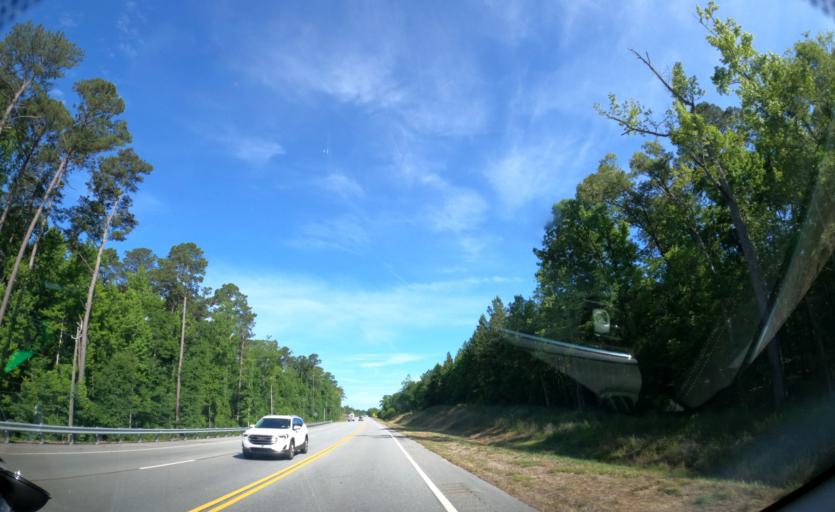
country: US
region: Georgia
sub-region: Columbia County
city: Appling
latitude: 33.6462
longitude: -82.3131
